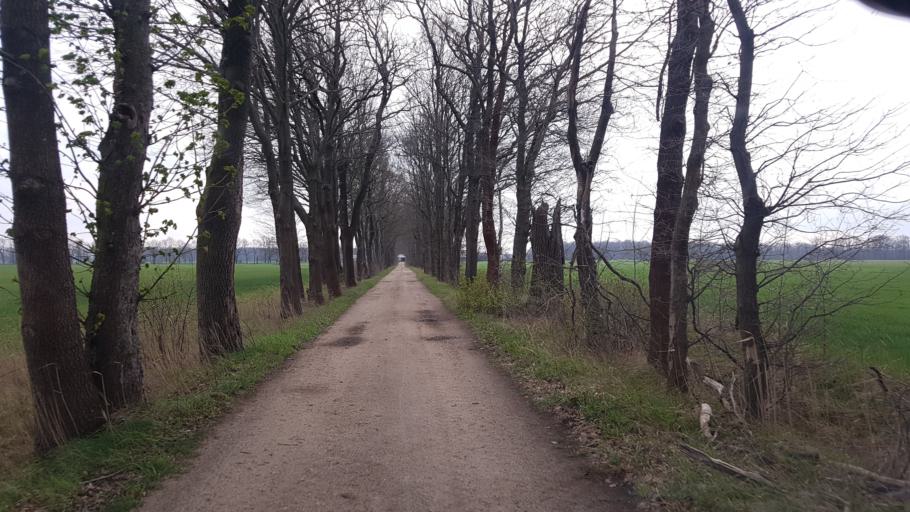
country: DE
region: Brandenburg
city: Bronkow
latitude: 51.6198
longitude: 13.9042
